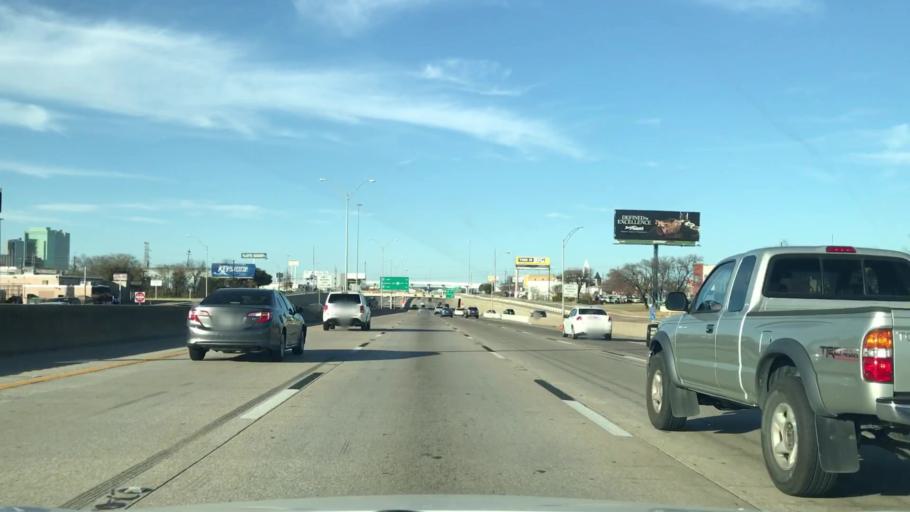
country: US
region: Texas
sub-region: Tarrant County
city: Fort Worth
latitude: 32.7340
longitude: -97.3205
